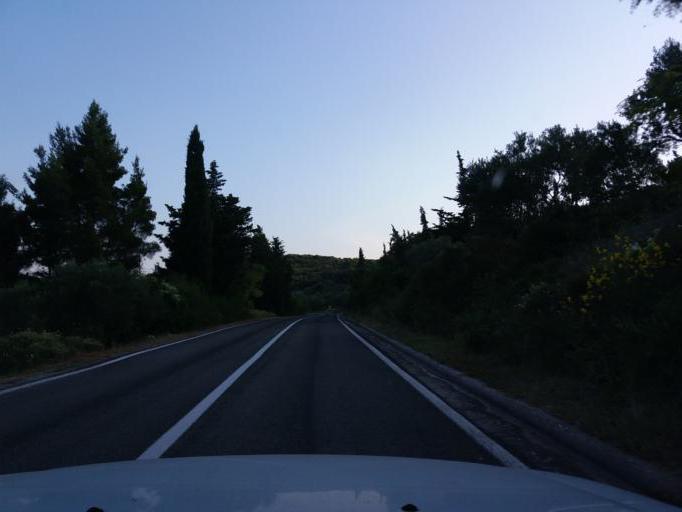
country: HR
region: Zadarska
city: Ugljan
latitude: 44.0812
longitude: 15.0012
